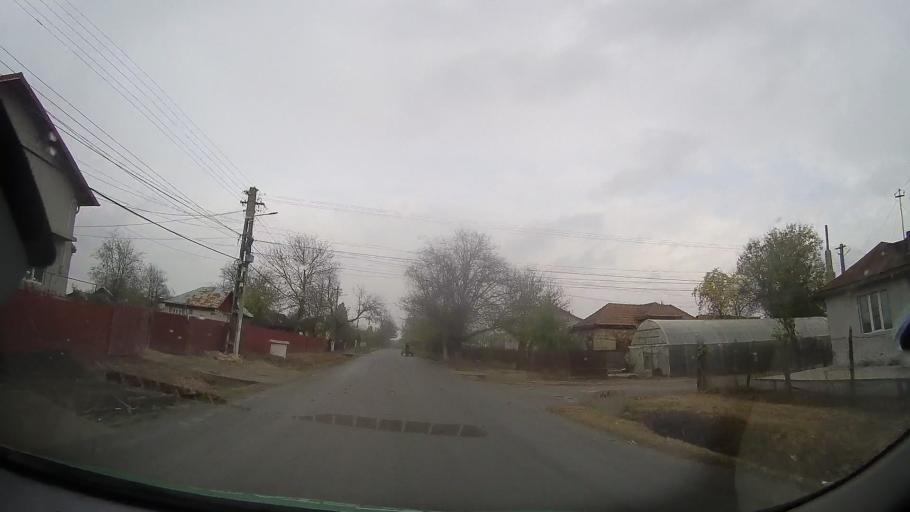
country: RO
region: Prahova
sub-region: Comuna Draganesti
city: Draganesti
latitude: 44.7990
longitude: 26.2885
